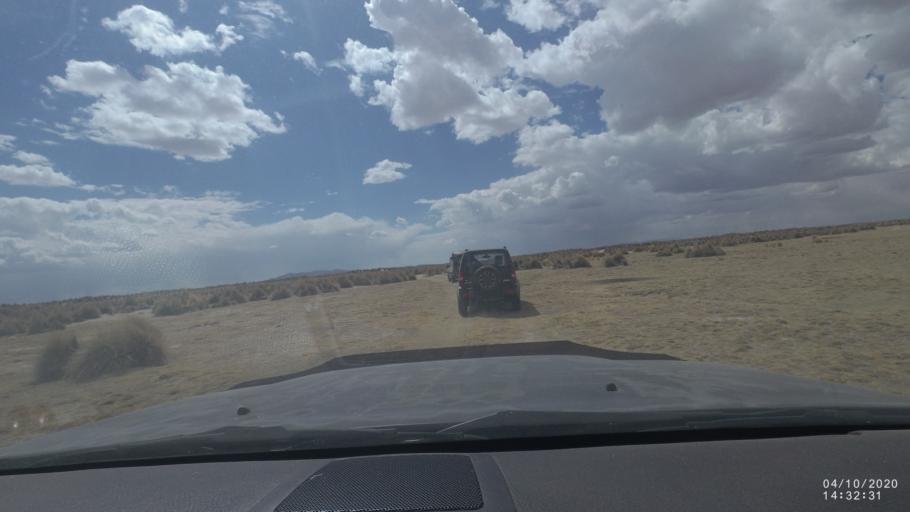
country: BO
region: Oruro
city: Poopo
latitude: -18.6730
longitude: -67.4651
